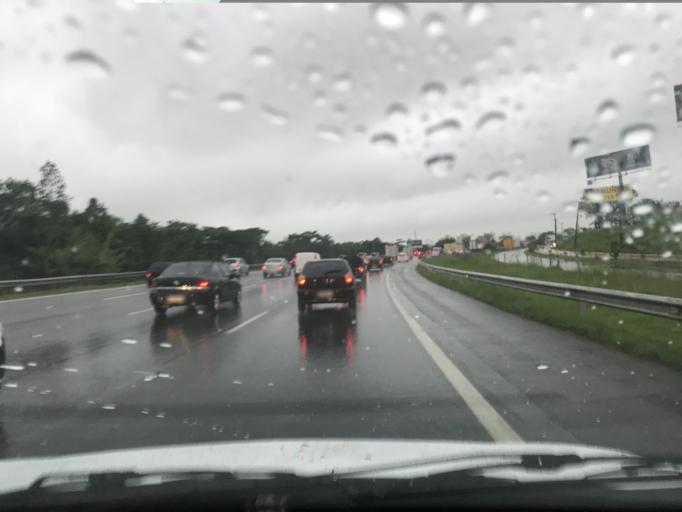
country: BR
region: Sao Paulo
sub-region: Guarulhos
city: Guarulhos
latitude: -23.5034
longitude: -46.5452
